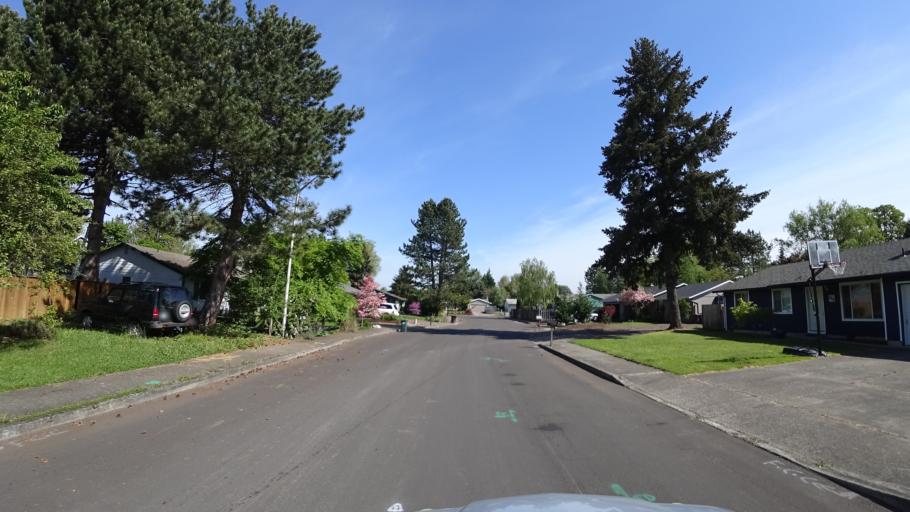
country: US
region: Oregon
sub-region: Washington County
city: Hillsboro
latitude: 45.5253
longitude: -122.9470
